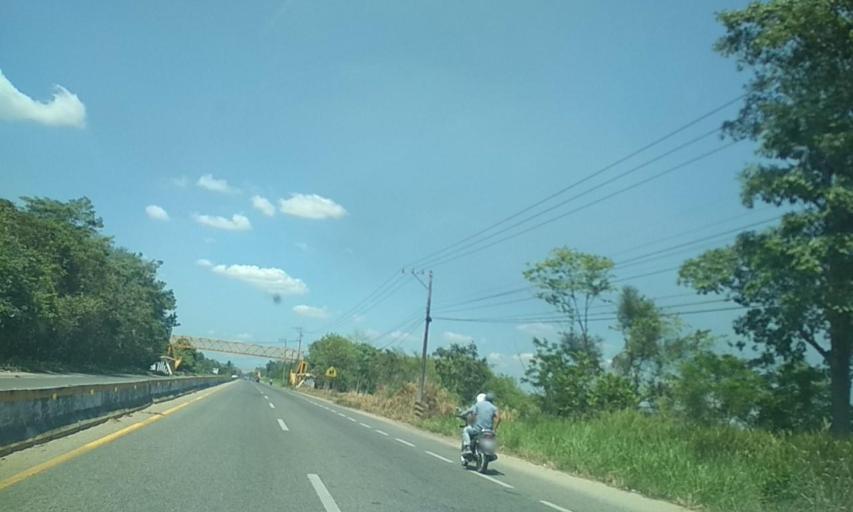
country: MX
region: Tabasco
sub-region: Huimanguillo
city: El Dorado
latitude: 17.8639
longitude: -93.3847
